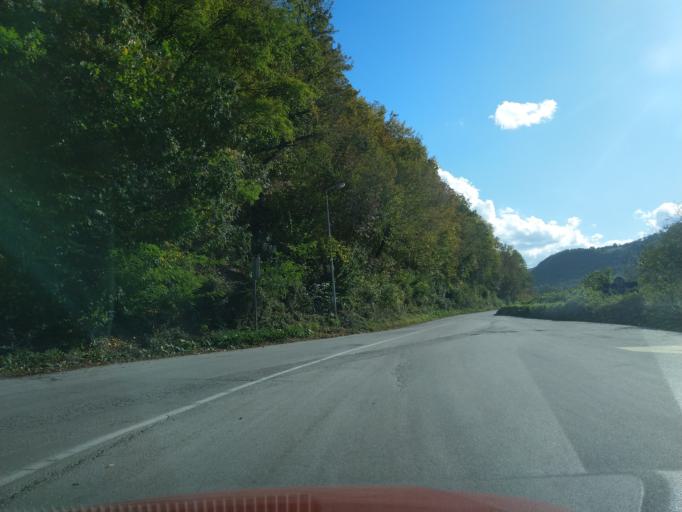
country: RS
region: Central Serbia
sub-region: Zlatiborski Okrug
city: Uzice
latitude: 43.8664
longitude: 19.8151
